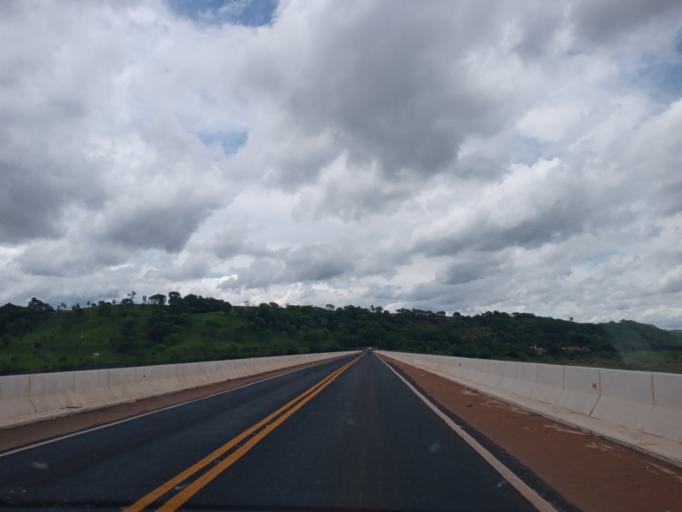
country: BR
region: Minas Gerais
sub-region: Monte Carmelo
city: Monte Carmelo
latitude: -19.2686
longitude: -47.6376
